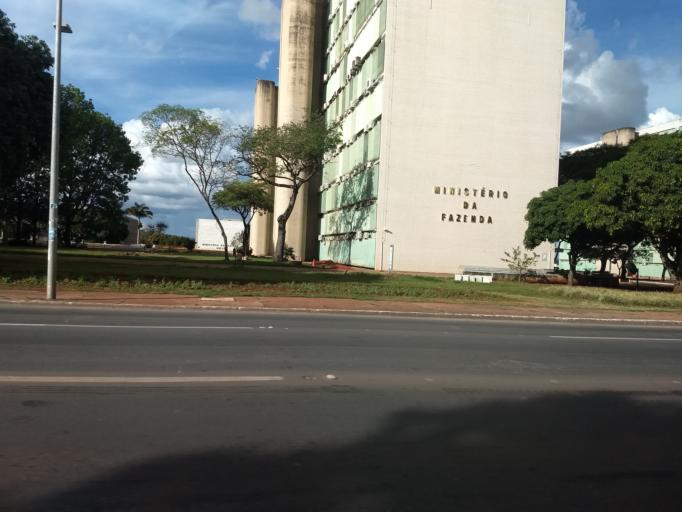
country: BR
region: Federal District
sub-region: Brasilia
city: Brasilia
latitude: -15.7967
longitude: -47.8702
